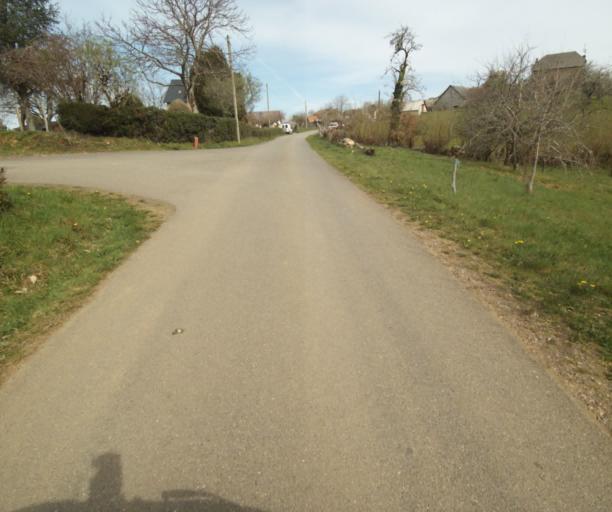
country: FR
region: Limousin
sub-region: Departement de la Correze
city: Correze
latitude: 45.3575
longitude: 1.8150
